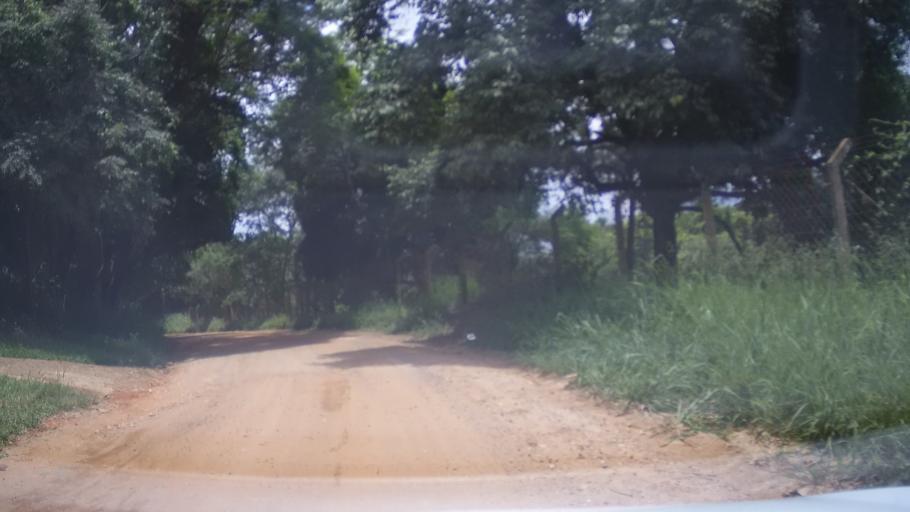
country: BR
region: Sao Paulo
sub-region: Vinhedo
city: Vinhedo
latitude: -23.0004
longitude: -46.9577
